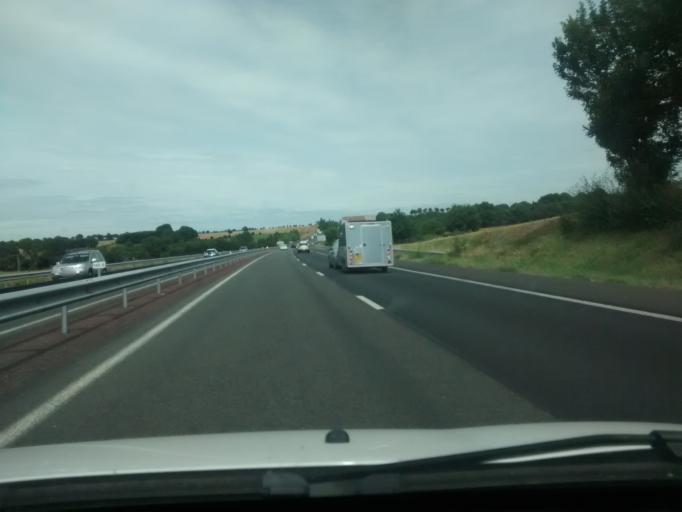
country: FR
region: Lower Normandy
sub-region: Departement de la Manche
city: Saint-James
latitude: 48.5152
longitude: -1.3483
